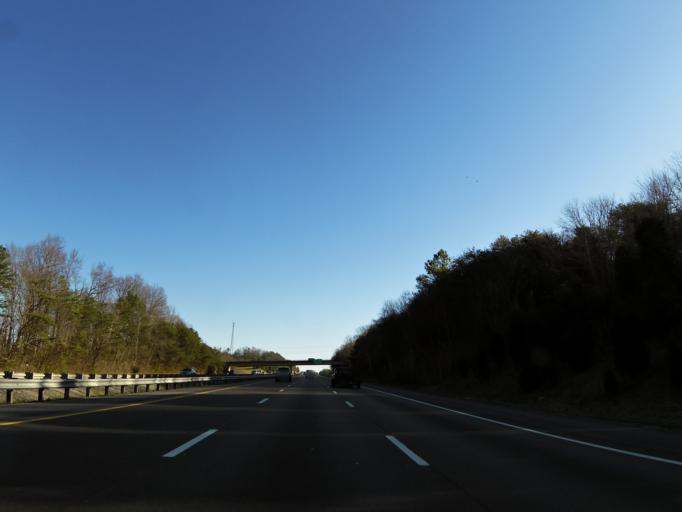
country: US
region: Tennessee
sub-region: Jefferson County
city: Dandridge
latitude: 36.0207
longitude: -83.4846
